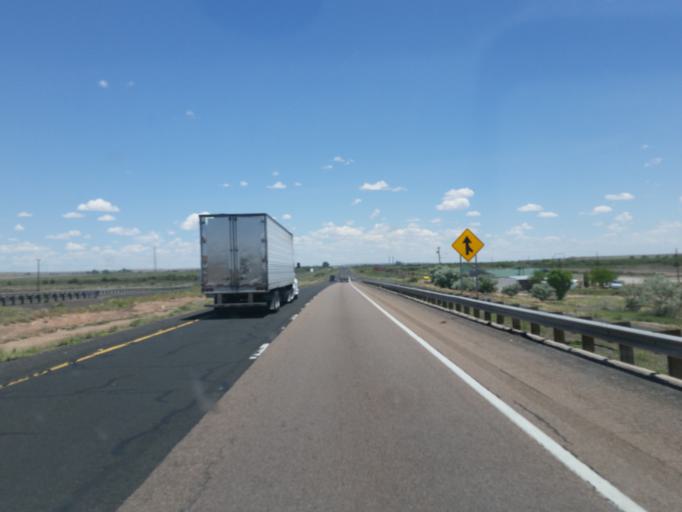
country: US
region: Arizona
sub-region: Navajo County
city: Joseph City
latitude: 34.9689
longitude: -110.4327
